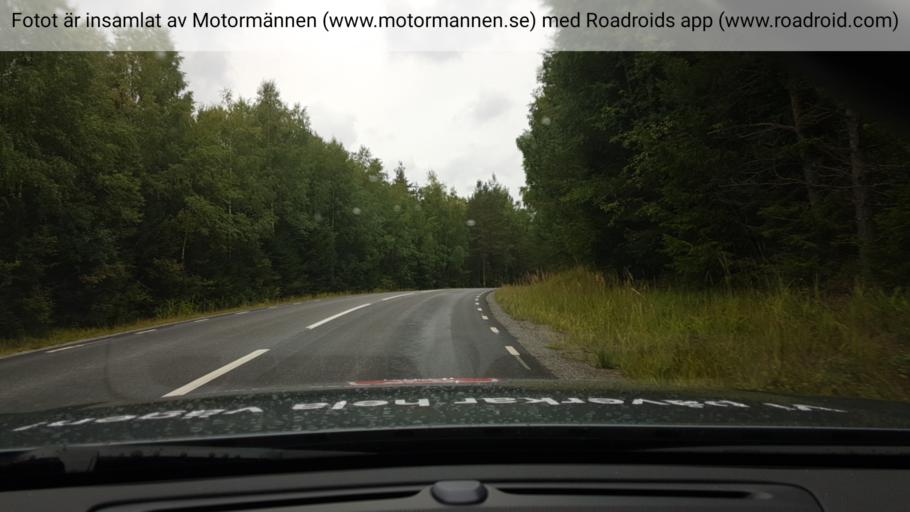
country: SE
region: Stockholm
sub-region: Botkyrka Kommun
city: Tullinge
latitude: 59.1437
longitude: 17.9345
